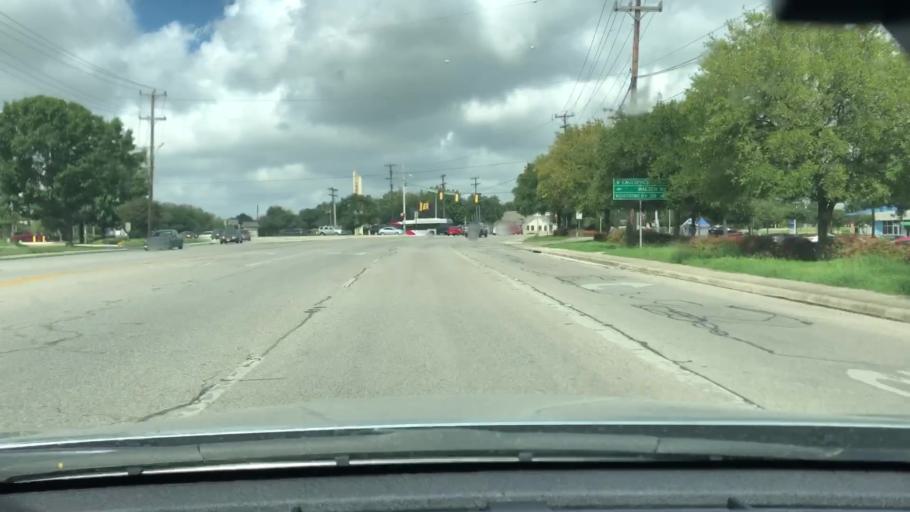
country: US
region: Texas
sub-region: Bexar County
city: Windcrest
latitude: 29.5093
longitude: -98.3709
